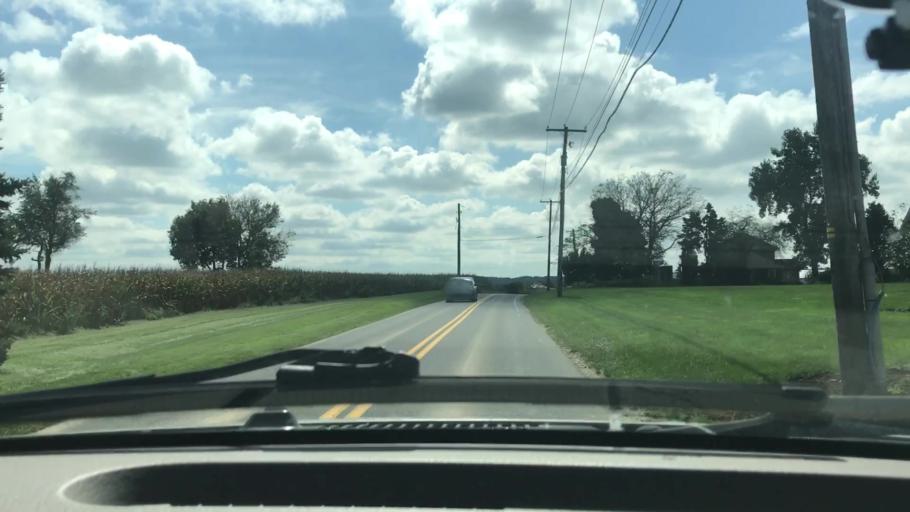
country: US
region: Pennsylvania
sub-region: Lancaster County
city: Landisville
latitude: 40.1112
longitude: -76.3861
